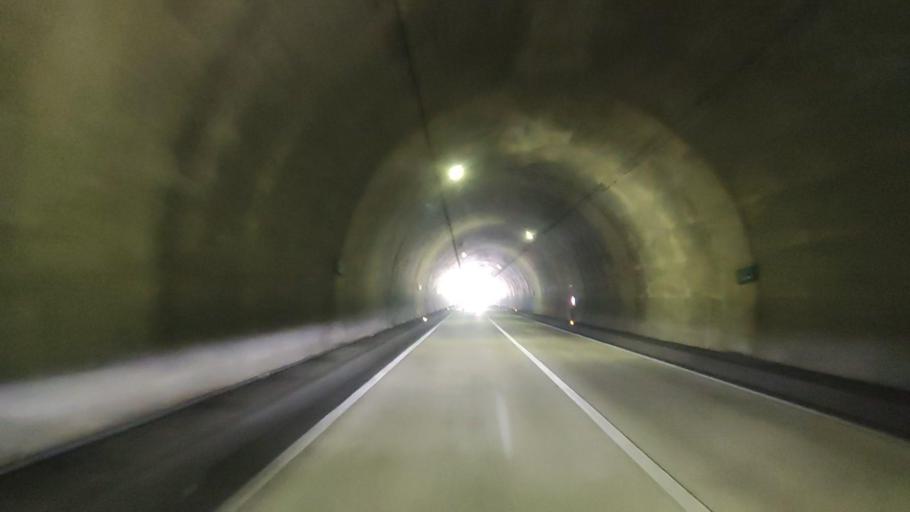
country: JP
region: Nara
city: Yoshino-cho
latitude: 34.2118
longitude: 135.9985
